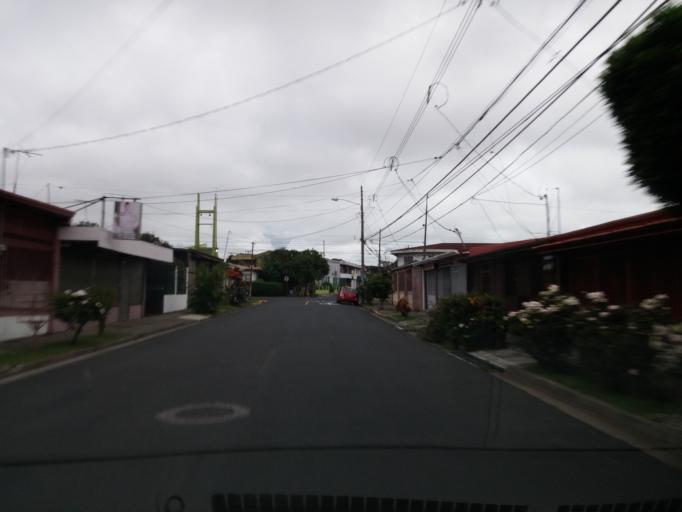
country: CR
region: Heredia
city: San Francisco
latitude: 10.0003
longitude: -84.1257
